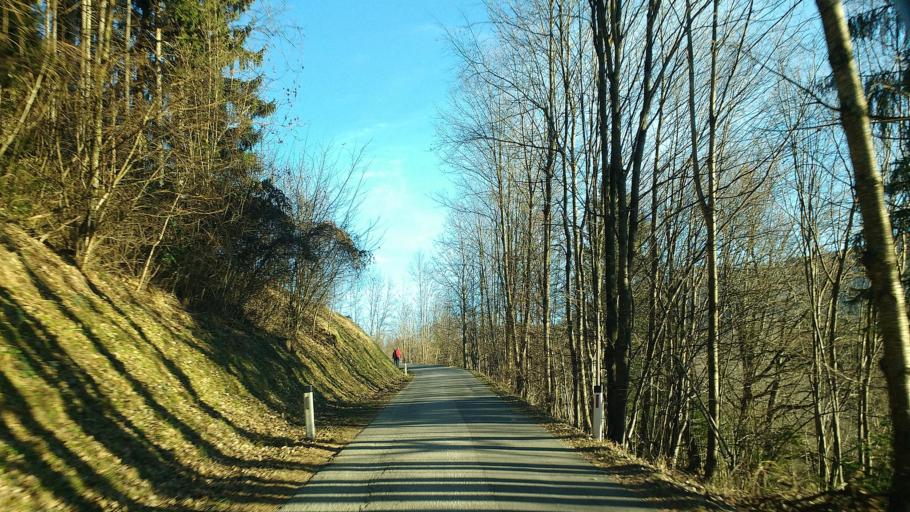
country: AT
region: Upper Austria
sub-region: Politischer Bezirk Kirchdorf an der Krems
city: Micheldorf in Oberoesterreich
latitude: 47.9046
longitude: 14.1557
